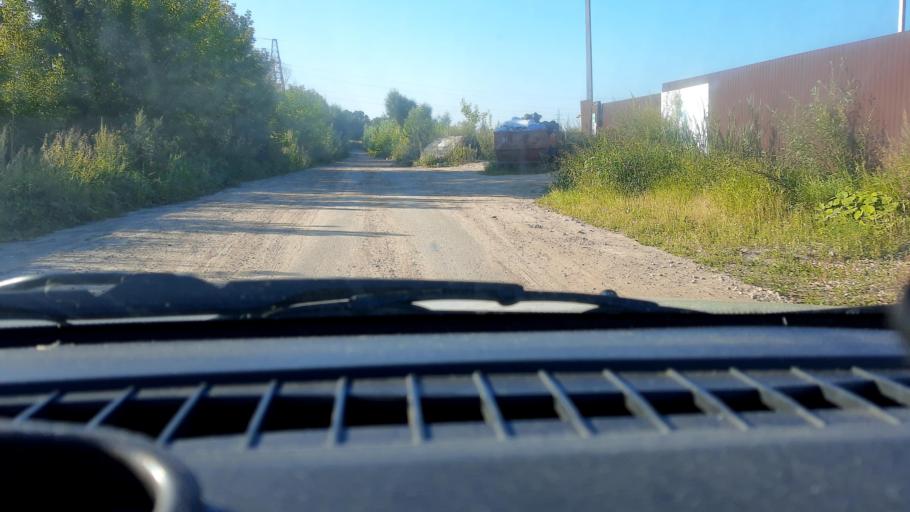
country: RU
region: Nizjnij Novgorod
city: Afonino
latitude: 56.2919
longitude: 44.1074
